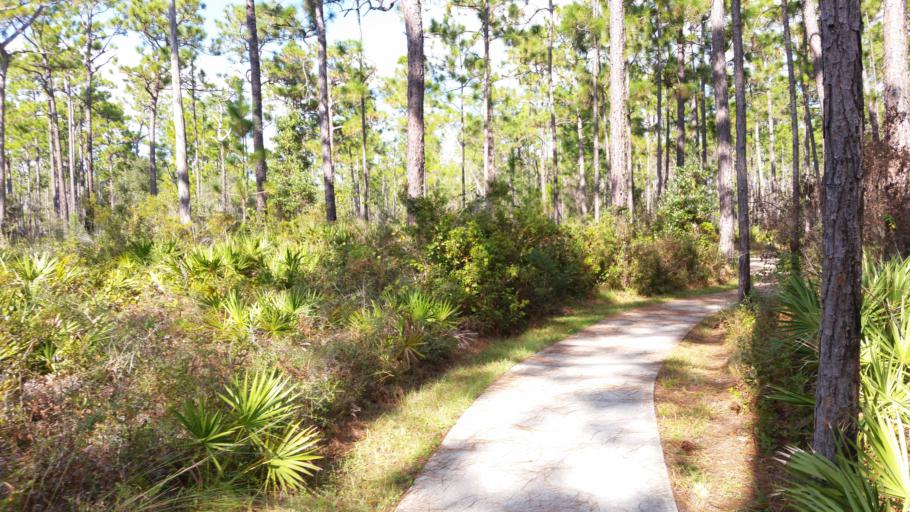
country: US
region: Florida
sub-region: Escambia County
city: Myrtle Grove
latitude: 30.3722
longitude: -87.4043
